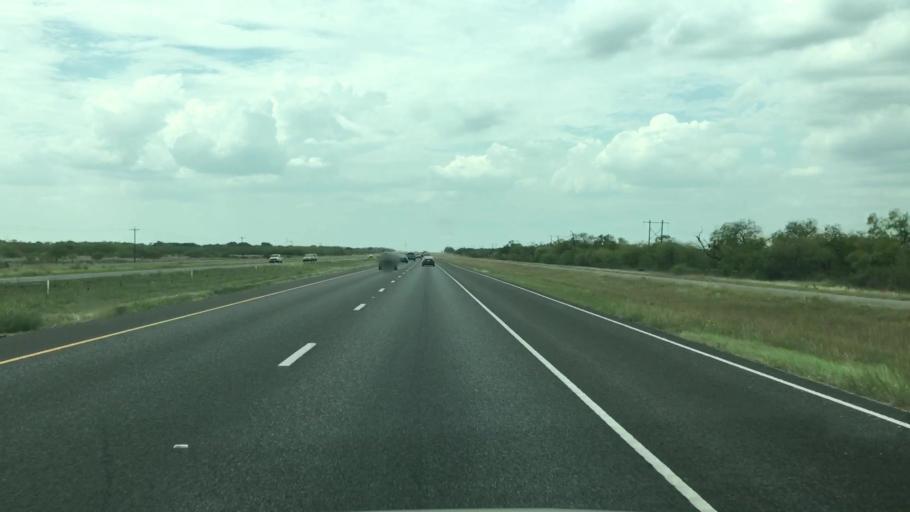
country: US
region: Texas
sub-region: Atascosa County
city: Pleasanton
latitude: 28.8027
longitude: -98.3436
